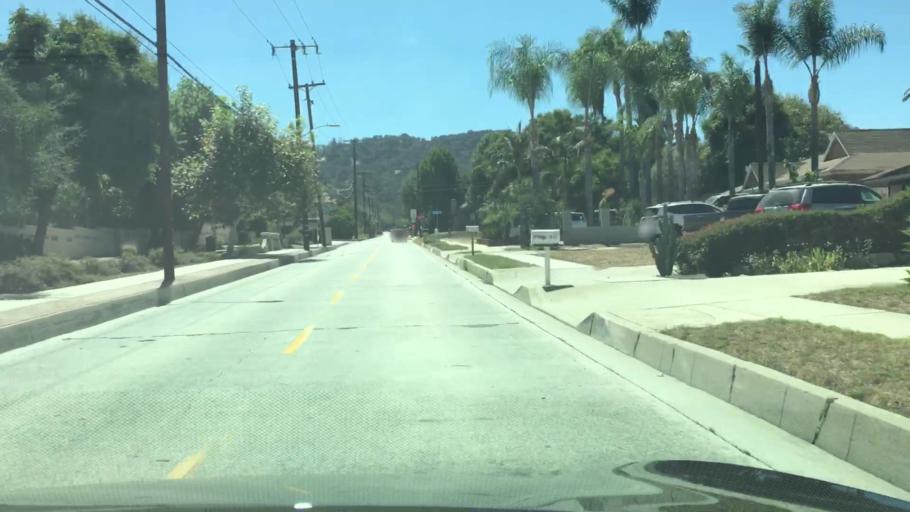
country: US
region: California
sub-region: Los Angeles County
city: Avocado Heights
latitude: 34.0140
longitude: -117.9913
